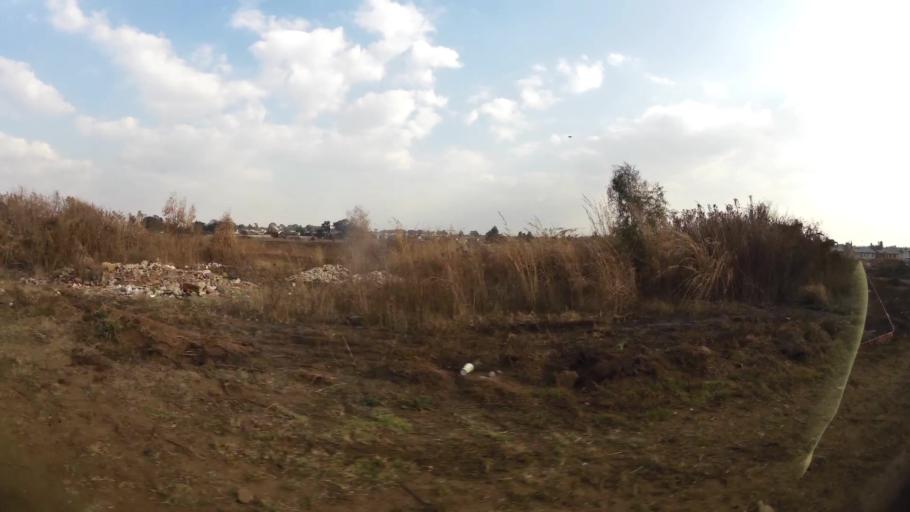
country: ZA
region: Gauteng
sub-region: Ekurhuleni Metropolitan Municipality
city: Benoni
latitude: -26.1051
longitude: 28.2938
